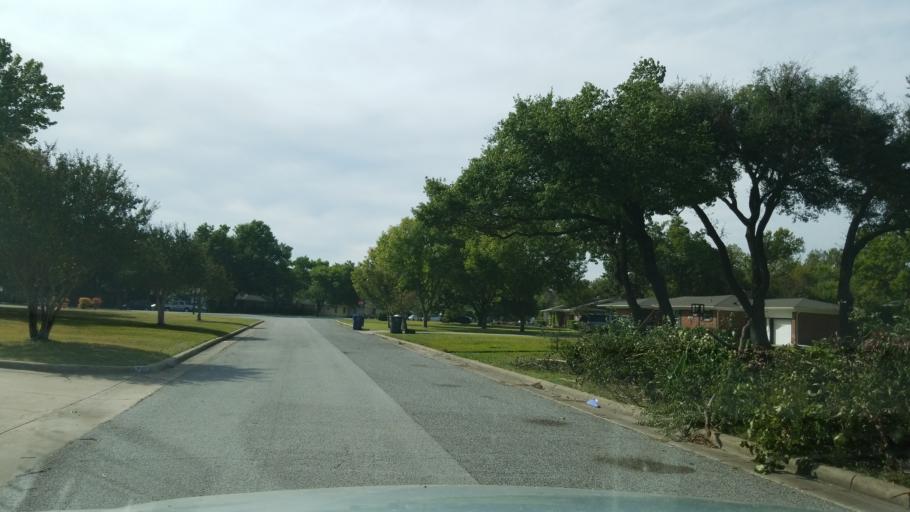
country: US
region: Texas
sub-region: Dallas County
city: Garland
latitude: 32.8992
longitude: -96.6513
